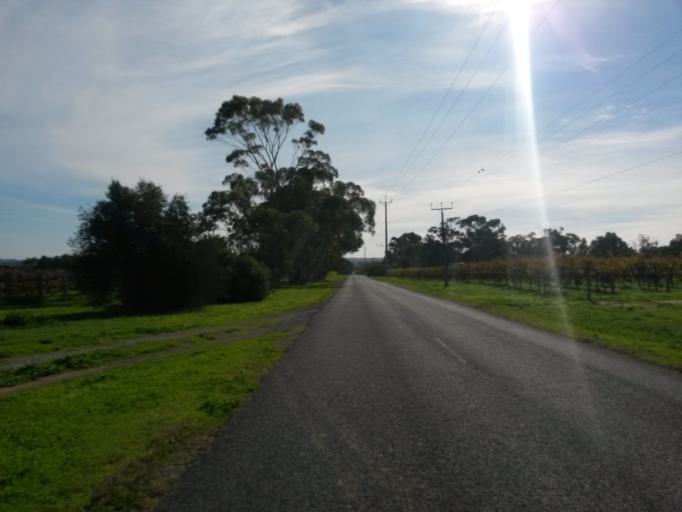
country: AU
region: South Australia
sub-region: Onkaparinga
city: McLaren Vale
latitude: -35.2354
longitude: 138.5706
